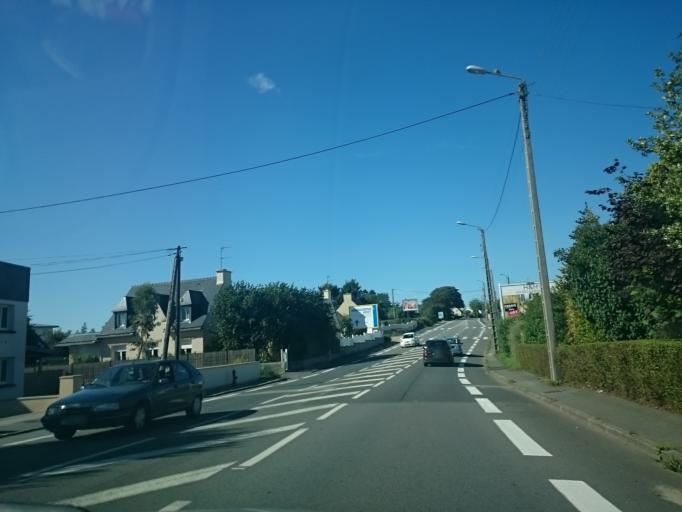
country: FR
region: Brittany
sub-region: Departement du Finistere
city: Brest
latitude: 48.4197
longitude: -4.4871
